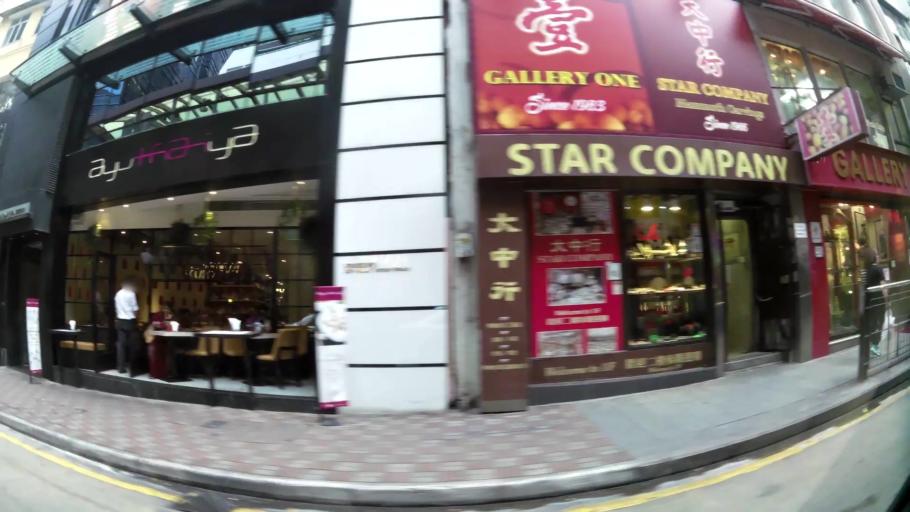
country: HK
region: Central and Western
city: Central
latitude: 22.2826
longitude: 114.1530
